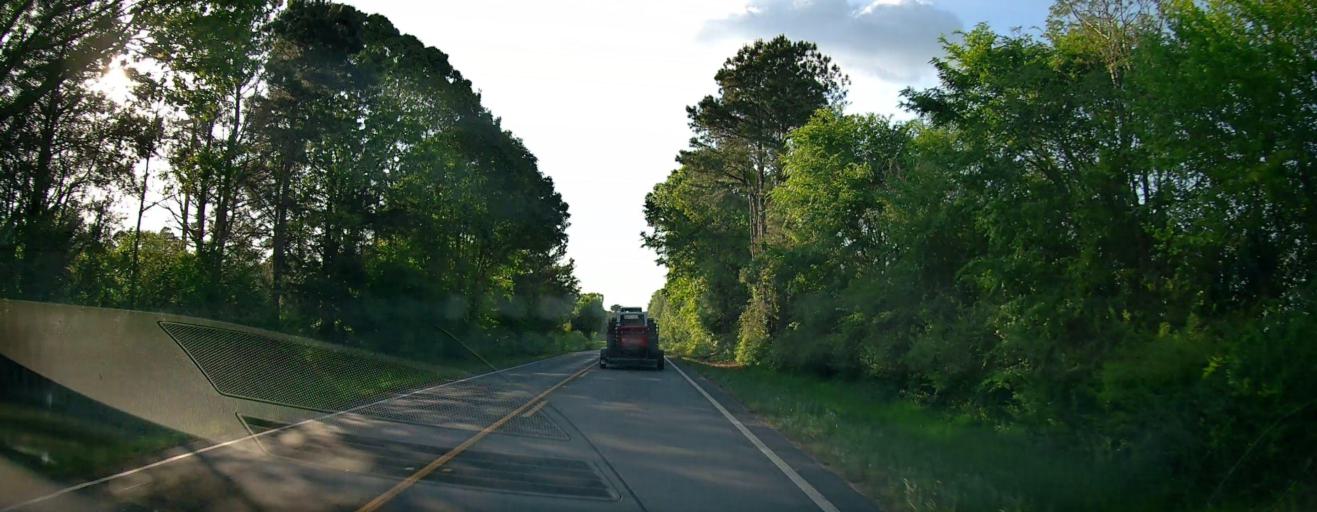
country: US
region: Georgia
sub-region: Putnam County
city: Eatonton
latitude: 33.3304
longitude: -83.5040
